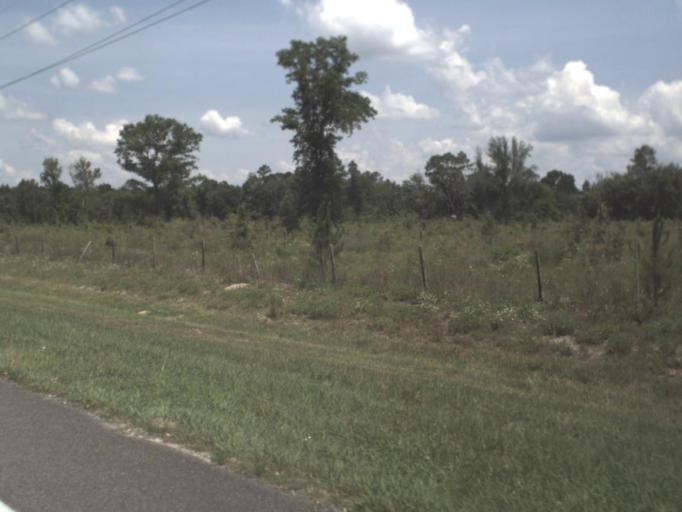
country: US
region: Florida
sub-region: Union County
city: Lake Butler
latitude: 30.0029
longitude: -82.2831
